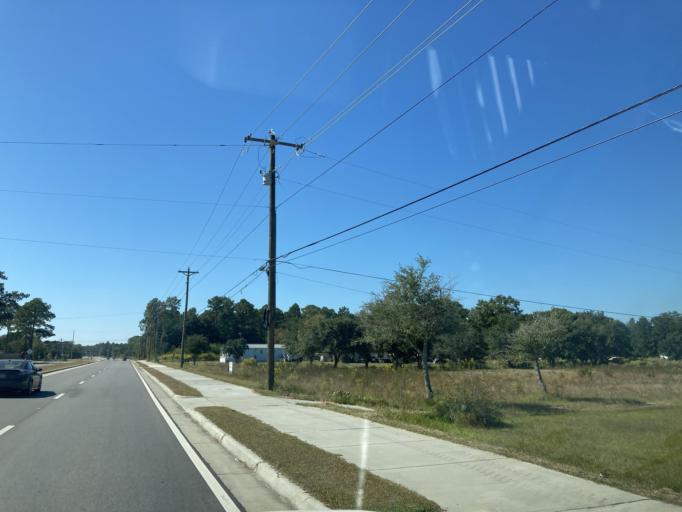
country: US
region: Mississippi
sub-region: Jackson County
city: Saint Martin
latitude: 30.4576
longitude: -88.8608
